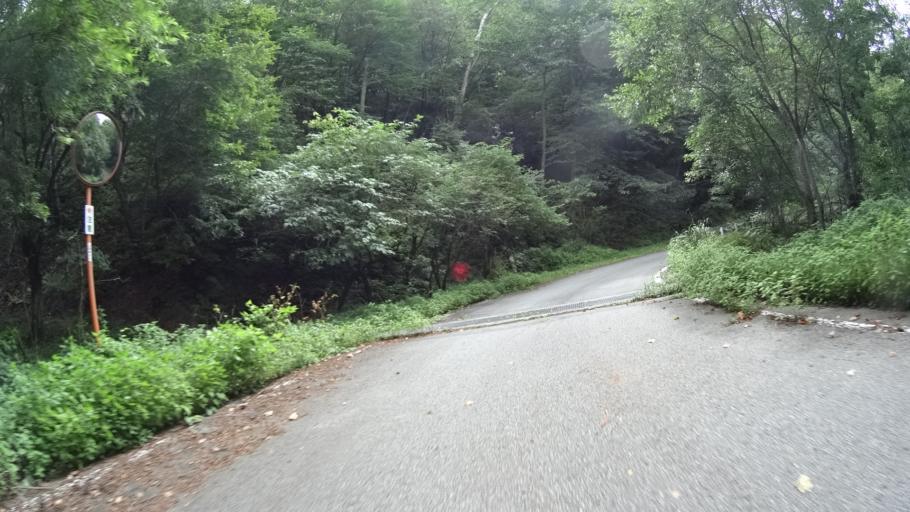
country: JP
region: Yamanashi
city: Nirasaki
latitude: 35.8048
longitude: 138.5454
